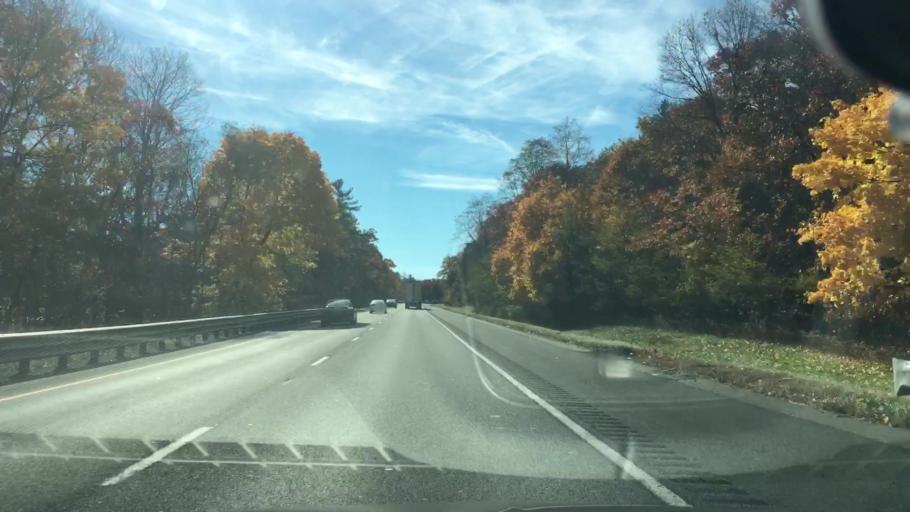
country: US
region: Massachusetts
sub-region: Hampden County
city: Holyoke
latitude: 42.2504
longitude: -72.6236
